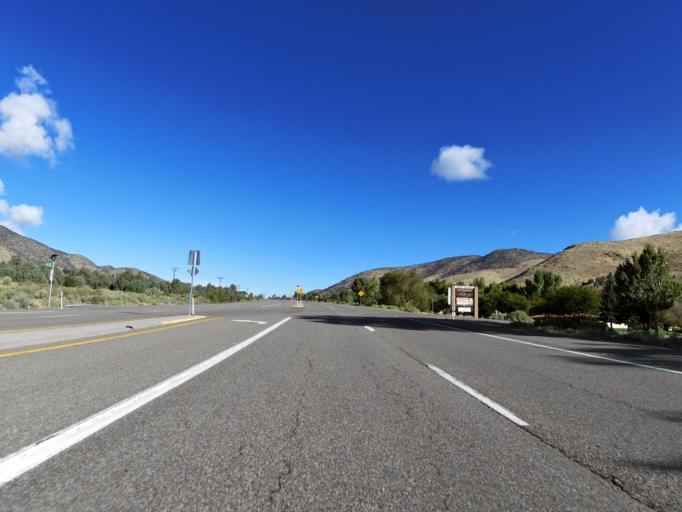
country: US
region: Nevada
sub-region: Lyon County
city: Smith Valley
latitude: 38.7318
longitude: -119.5566
